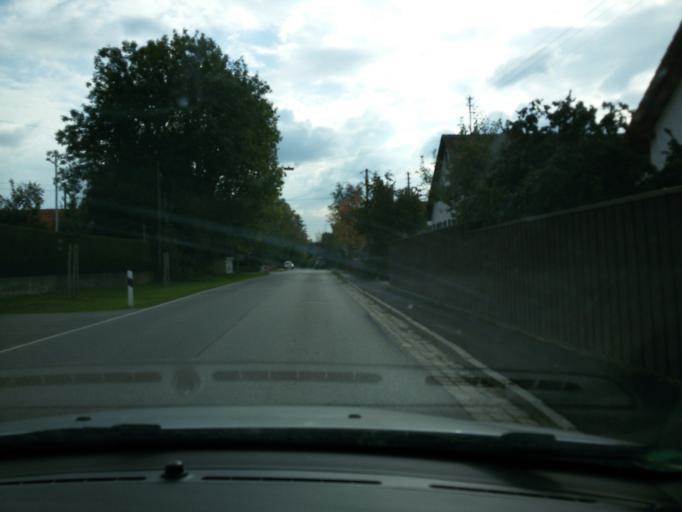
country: DE
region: Bavaria
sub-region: Swabia
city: Buchloe
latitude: 48.0631
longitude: 10.7309
